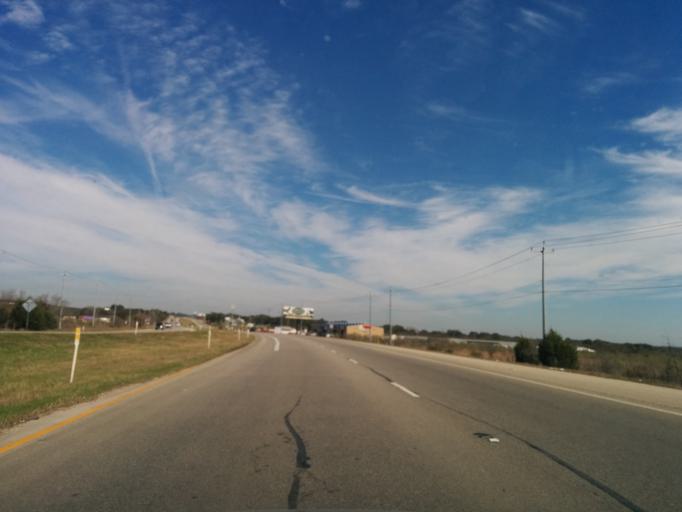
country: US
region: Texas
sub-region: Comal County
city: Bulverde
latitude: 29.7219
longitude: -98.4425
